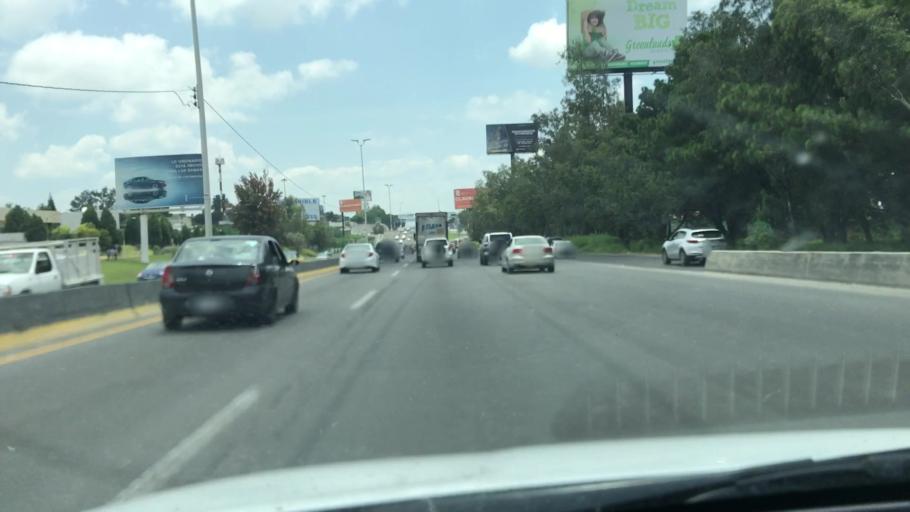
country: MX
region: Jalisco
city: Zapopan2
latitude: 20.7215
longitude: -103.4223
